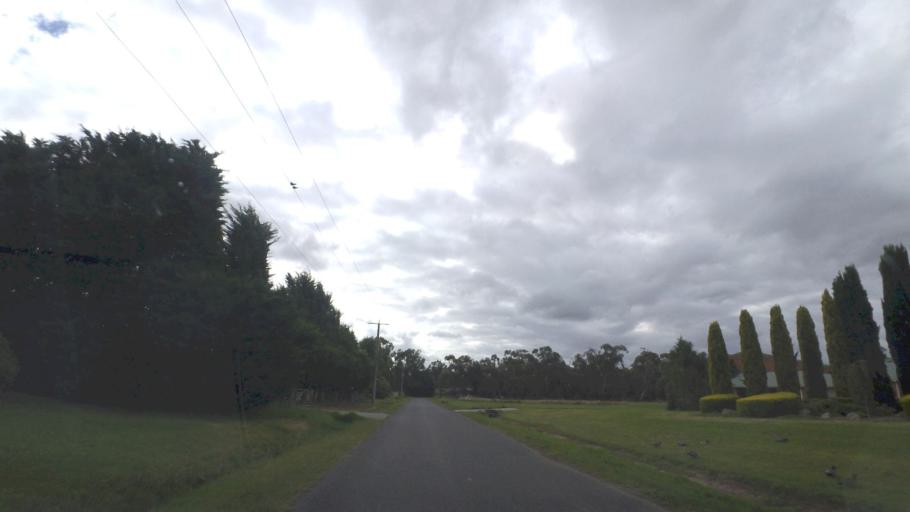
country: AU
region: Victoria
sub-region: Maroondah
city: Kilsyth South
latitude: -37.8251
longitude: 145.3128
